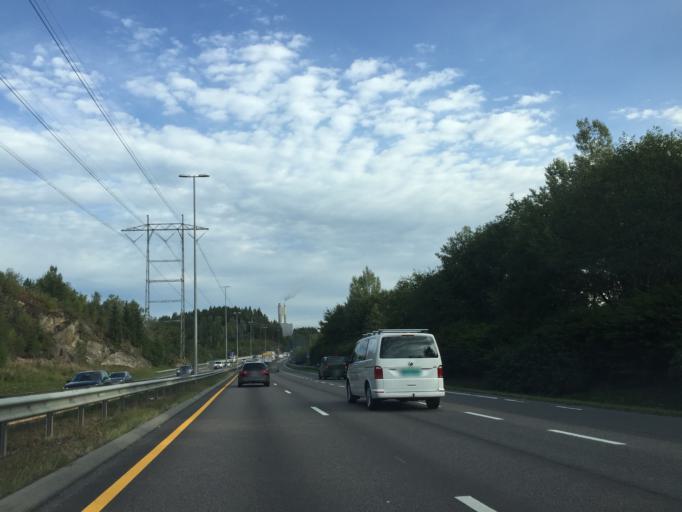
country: NO
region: Akershus
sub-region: Oppegard
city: Kolbotn
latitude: 59.8321
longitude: 10.8412
